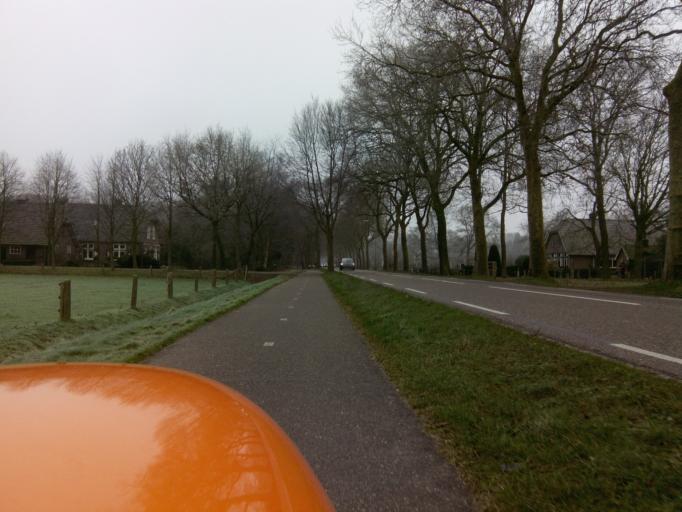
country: NL
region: Gelderland
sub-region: Gemeente Barneveld
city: Voorthuizen
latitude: 52.1976
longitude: 5.6079
